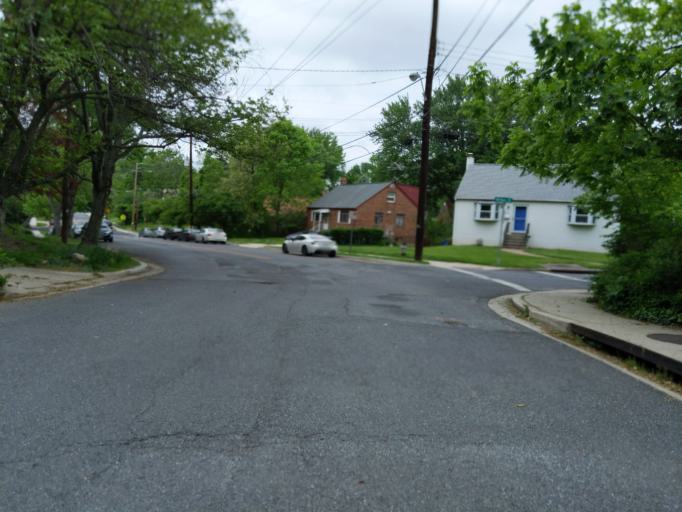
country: US
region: Maryland
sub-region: Montgomery County
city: Forest Glen
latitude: 39.0185
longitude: -77.0499
